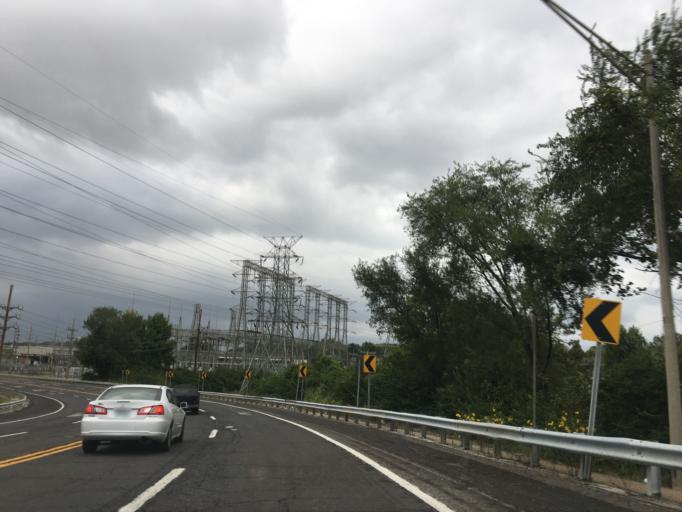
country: US
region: Missouri
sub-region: Saint Louis County
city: Berkeley
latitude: 38.7566
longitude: -90.3344
